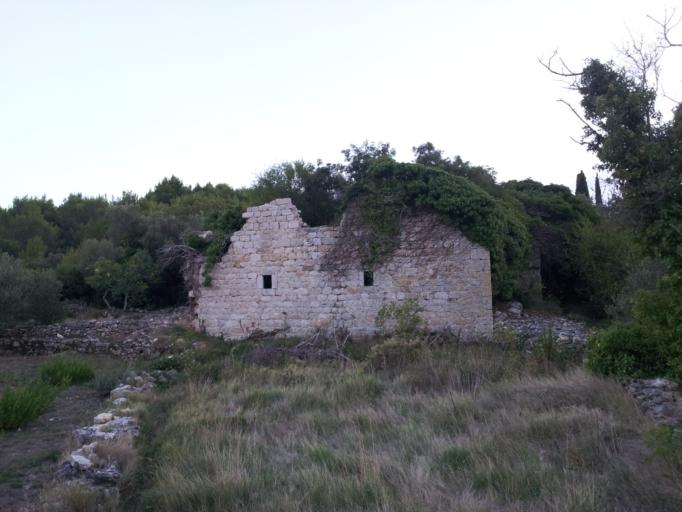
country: HR
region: Sibensko-Kniniska
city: Vodice
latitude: 43.7307
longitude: 15.7969
